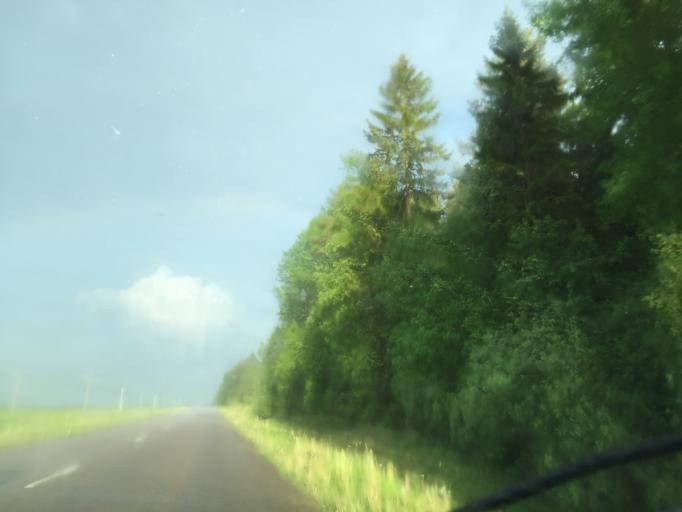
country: LT
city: Salantai
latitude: 56.0625
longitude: 21.4451
